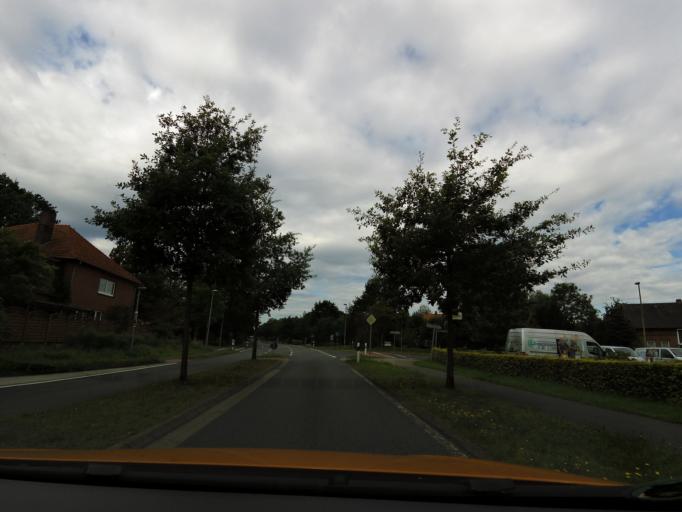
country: DE
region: Lower Saxony
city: Oldenburg
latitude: 53.1683
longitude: 8.1506
